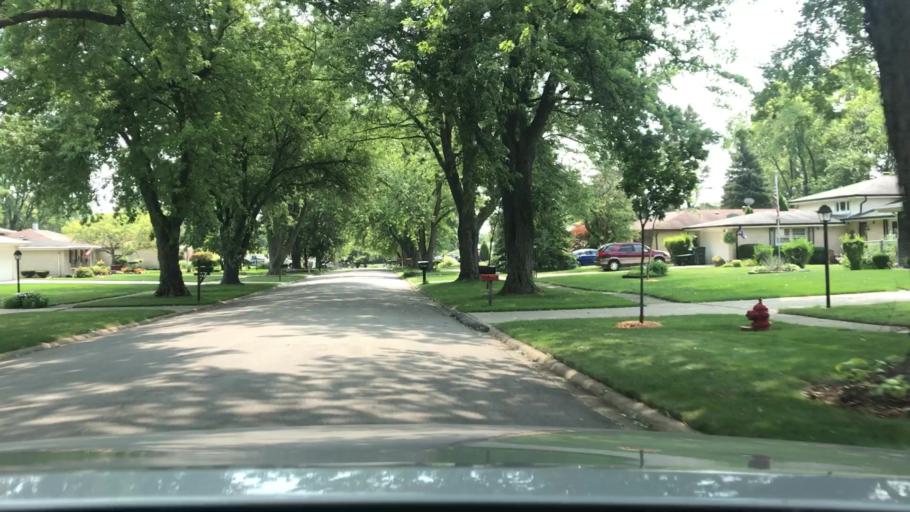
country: US
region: Illinois
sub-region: DuPage County
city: Darien
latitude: 41.7403
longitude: -87.9890
